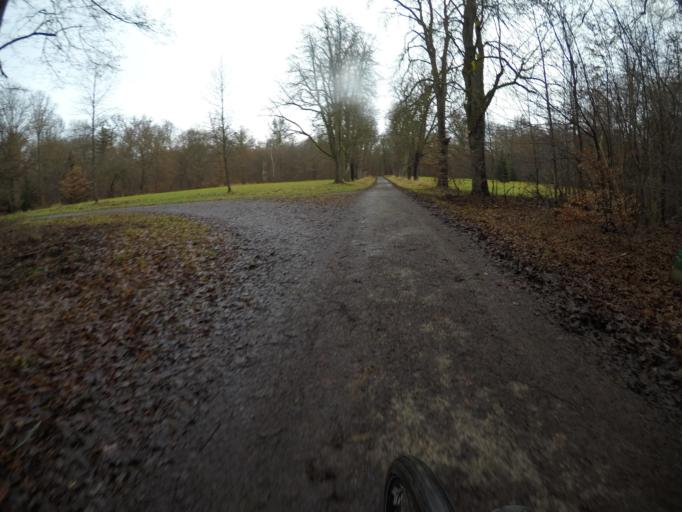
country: DE
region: Baden-Wuerttemberg
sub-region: Regierungsbezirk Stuttgart
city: Gerlingen
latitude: 48.7568
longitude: 9.0843
